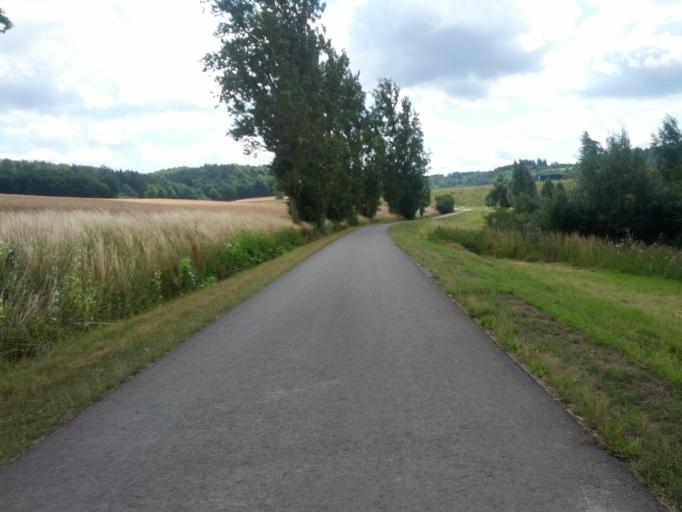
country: DE
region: Thuringia
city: Krauthausen
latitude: 51.0101
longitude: 10.2732
